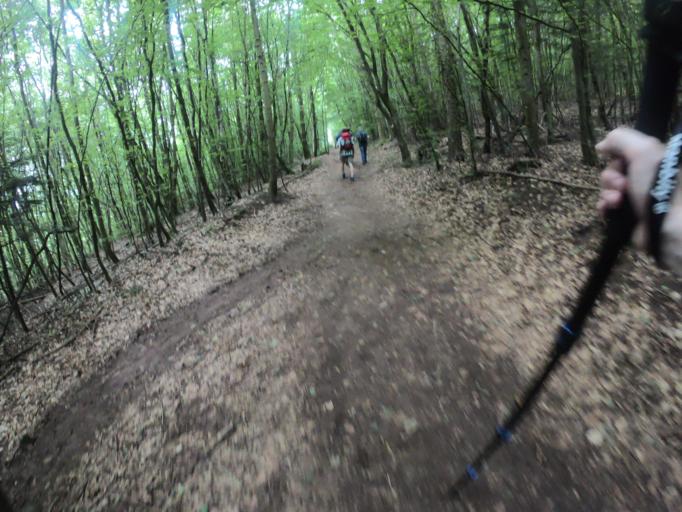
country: DE
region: Rheinland-Pfalz
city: Annweiler am Trifels
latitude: 49.1991
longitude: 7.9820
